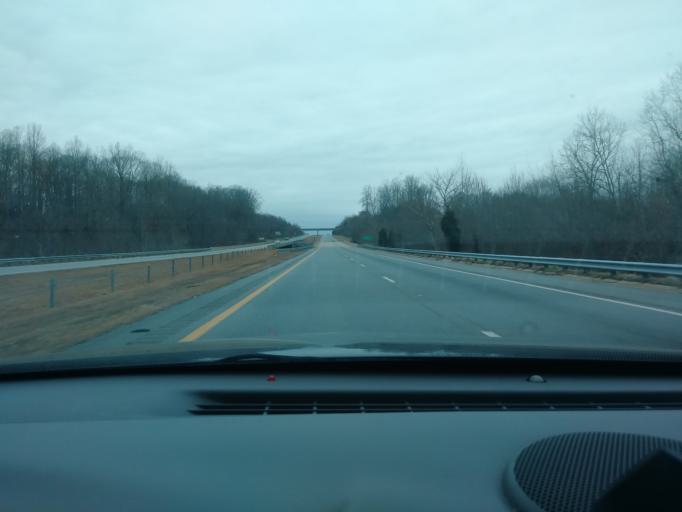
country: US
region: North Carolina
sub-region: Yadkin County
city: Yadkinville
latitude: 36.1186
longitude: -80.7208
